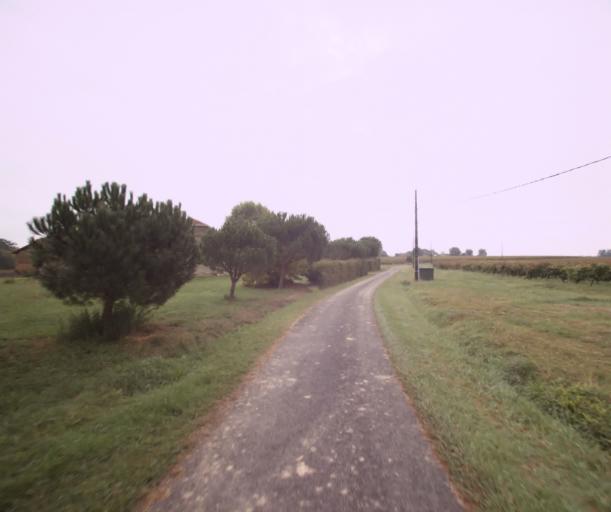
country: FR
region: Midi-Pyrenees
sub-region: Departement du Gers
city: Cazaubon
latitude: 43.9225
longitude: -0.1329
